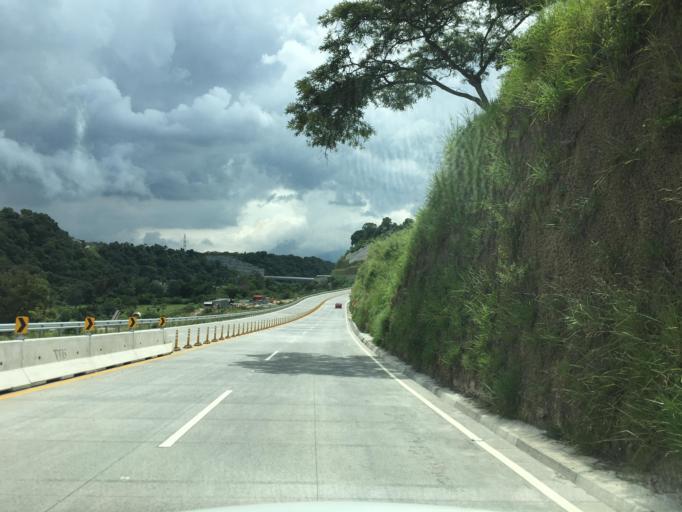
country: GT
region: Guatemala
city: Santa Catarina Pinula
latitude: 14.5457
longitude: -90.5324
